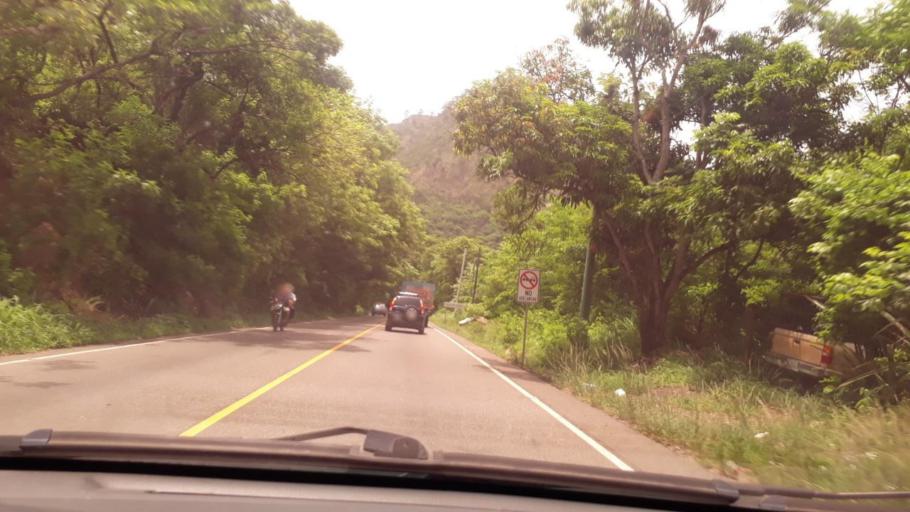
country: GT
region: Chiquimula
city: San Jacinto
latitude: 14.6500
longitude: -89.4846
